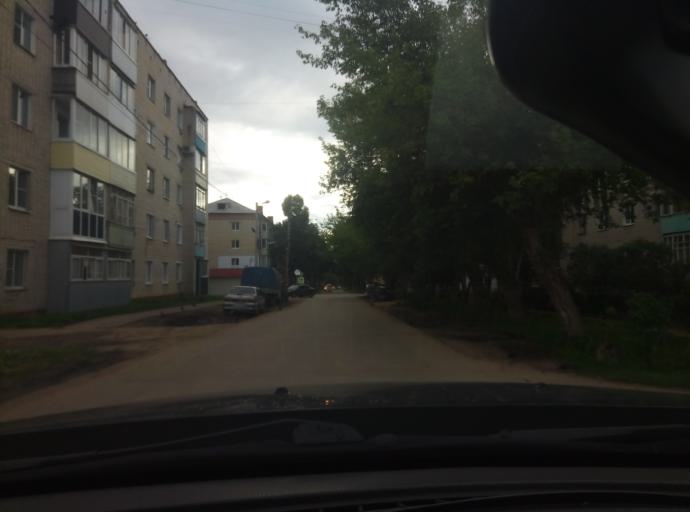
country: RU
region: Tula
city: Bolokhovo
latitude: 54.0849
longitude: 37.8326
